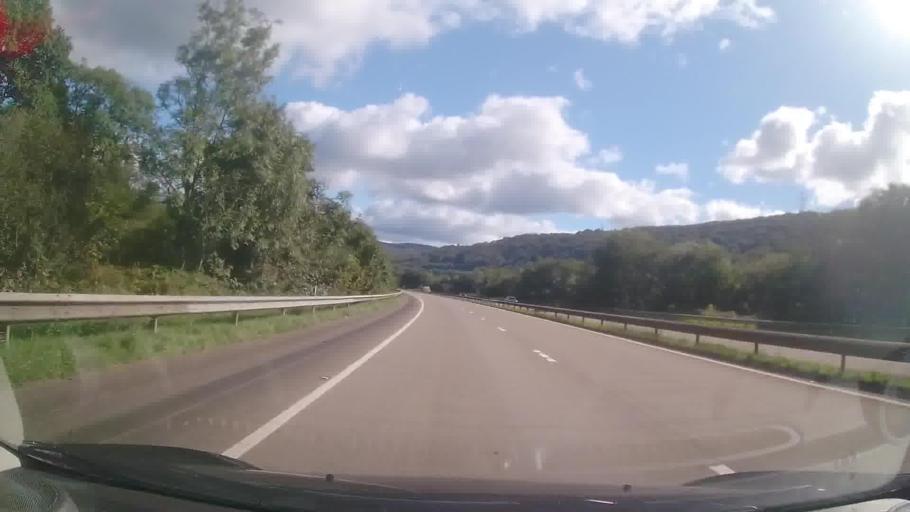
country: GB
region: Wales
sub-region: Neath Port Talbot
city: Neath
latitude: 51.6818
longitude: -3.7631
